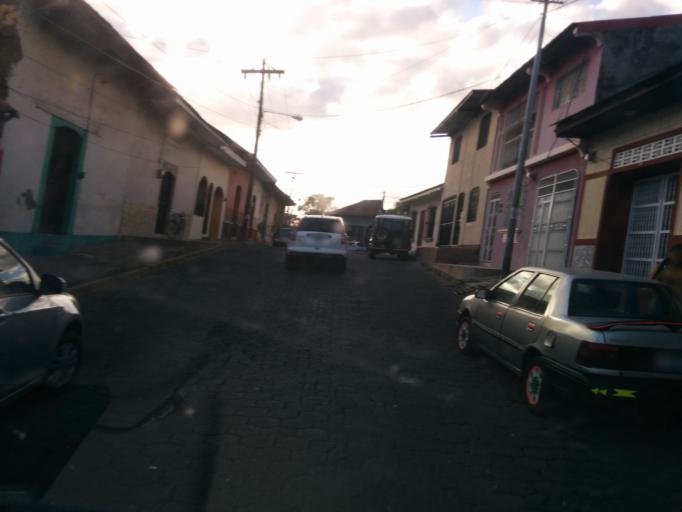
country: NI
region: Leon
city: Leon
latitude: 12.4333
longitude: -86.8785
